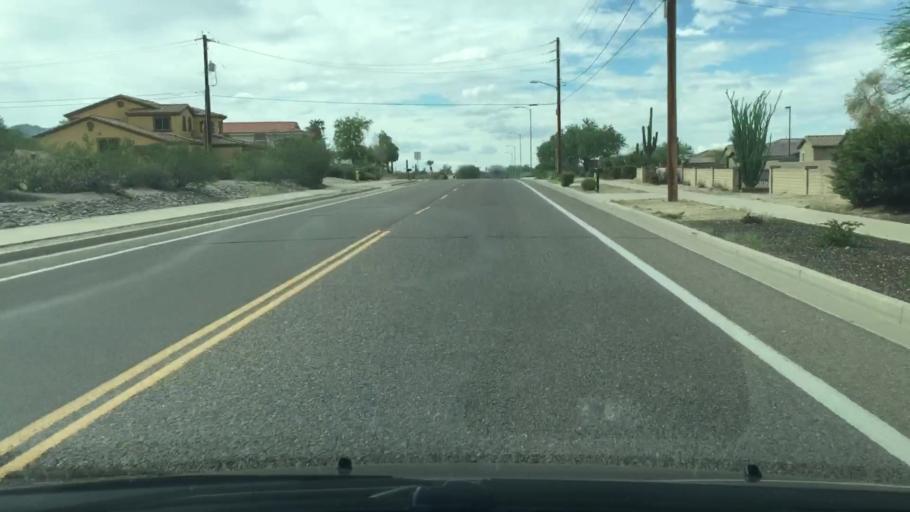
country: US
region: Arizona
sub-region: Maricopa County
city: Guadalupe
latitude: 33.3633
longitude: -112.0503
